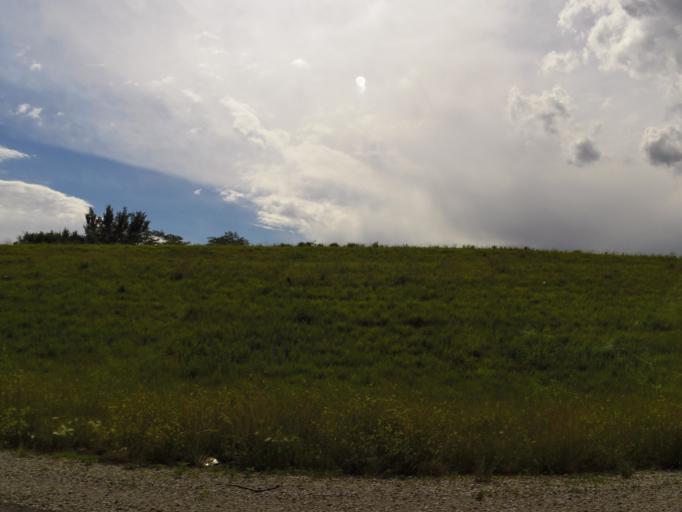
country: US
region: Iowa
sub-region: Henry County
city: Winfield
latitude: 41.2056
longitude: -91.5290
